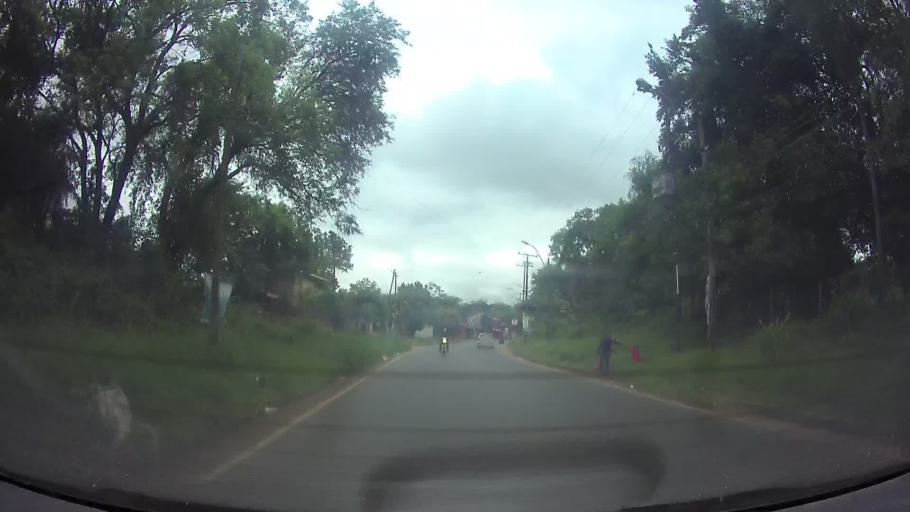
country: PY
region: Central
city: Nemby
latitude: -25.3814
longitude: -57.5470
